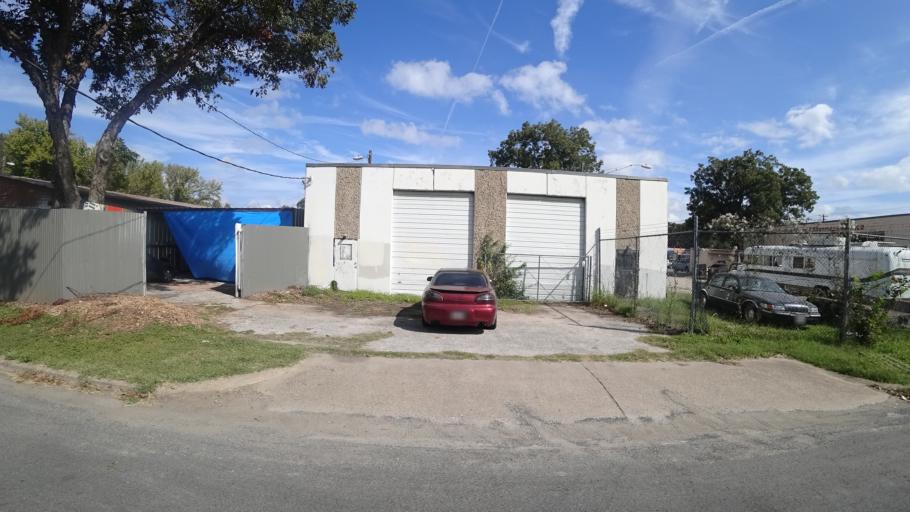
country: US
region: Texas
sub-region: Travis County
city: Austin
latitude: 30.2558
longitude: -97.7025
